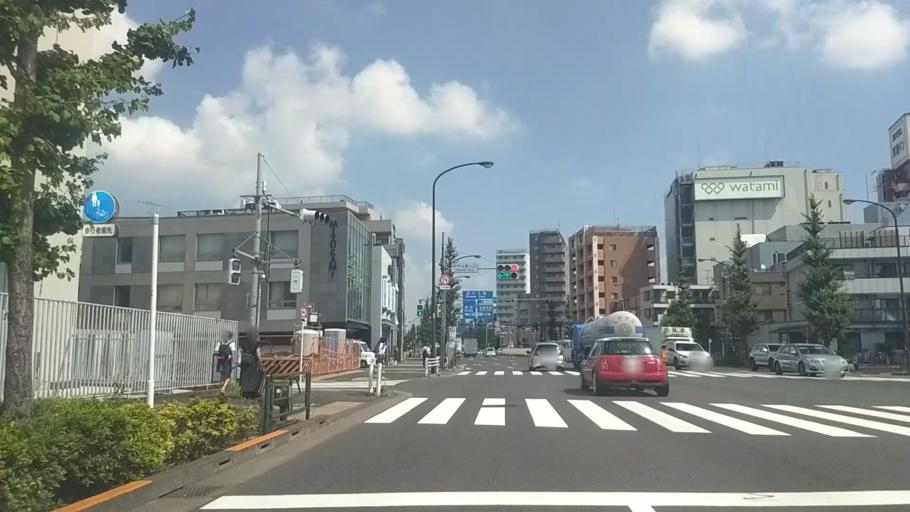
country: JP
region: Kanagawa
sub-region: Kawasaki-shi
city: Kawasaki
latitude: 35.5505
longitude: 139.7407
